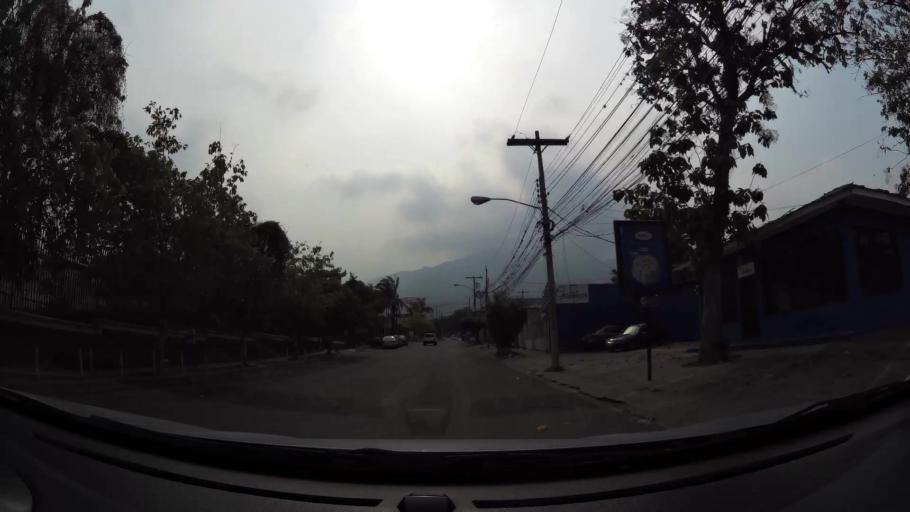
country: HN
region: Cortes
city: San Pedro Sula
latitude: 15.5019
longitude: -88.0347
